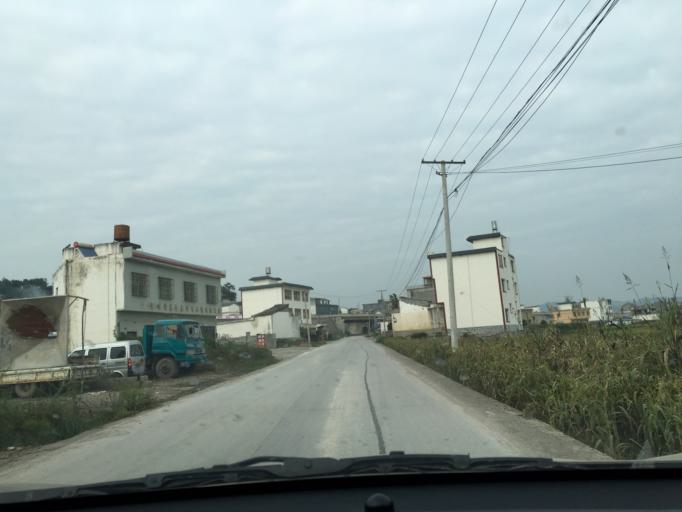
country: CN
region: Guangxi Zhuangzu Zizhiqu
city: Xinzhou
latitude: 25.4584
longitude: 105.4869
